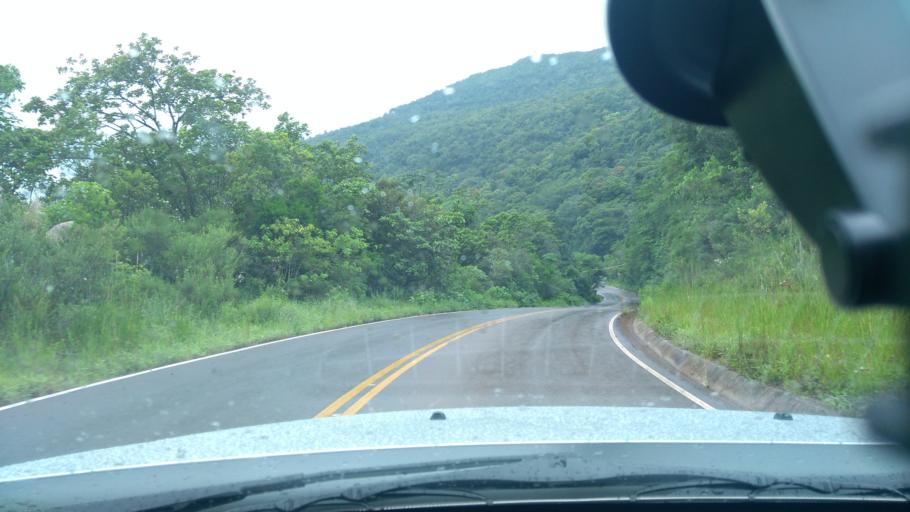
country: BR
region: Rio Grande do Sul
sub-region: Torres
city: Torres
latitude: -29.1844
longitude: -49.9870
